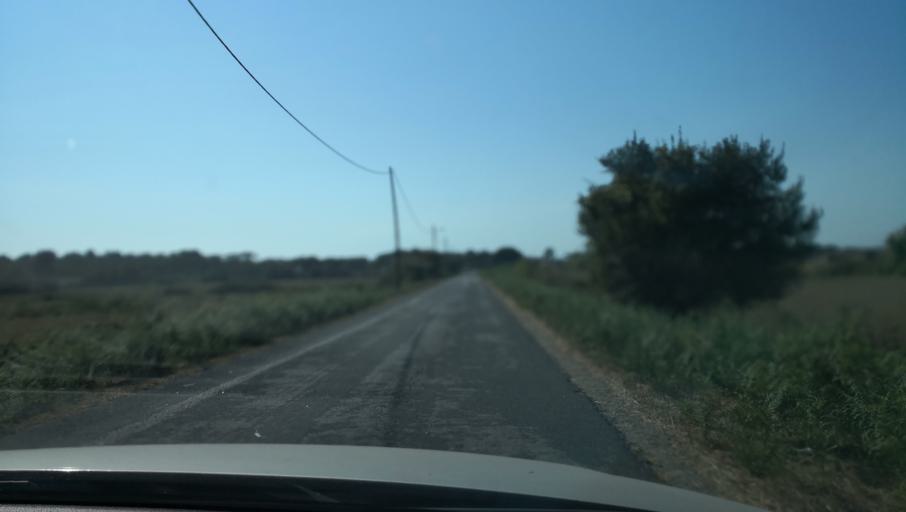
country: PT
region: Setubal
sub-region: Setubal
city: Setubal
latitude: 38.4023
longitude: -8.7565
